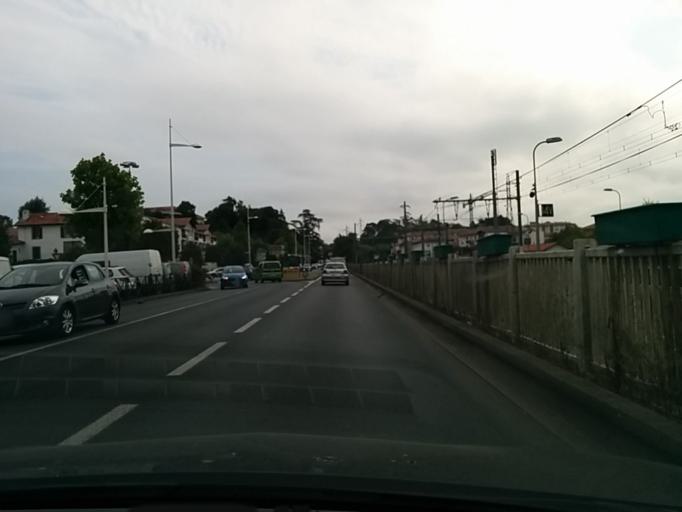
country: FR
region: Aquitaine
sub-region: Departement des Pyrenees-Atlantiques
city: Saint-Jean-de-Luz
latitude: 43.3865
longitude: -1.6593
